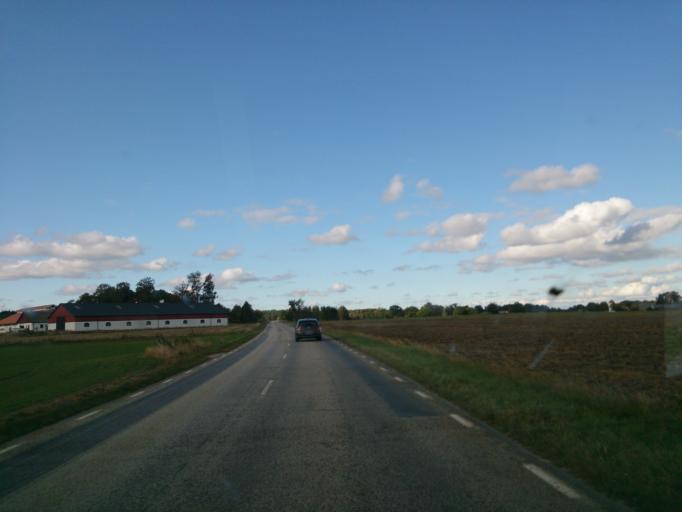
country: SE
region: Skane
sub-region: Sjobo Kommun
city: Blentarp
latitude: 55.5995
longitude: 13.5944
